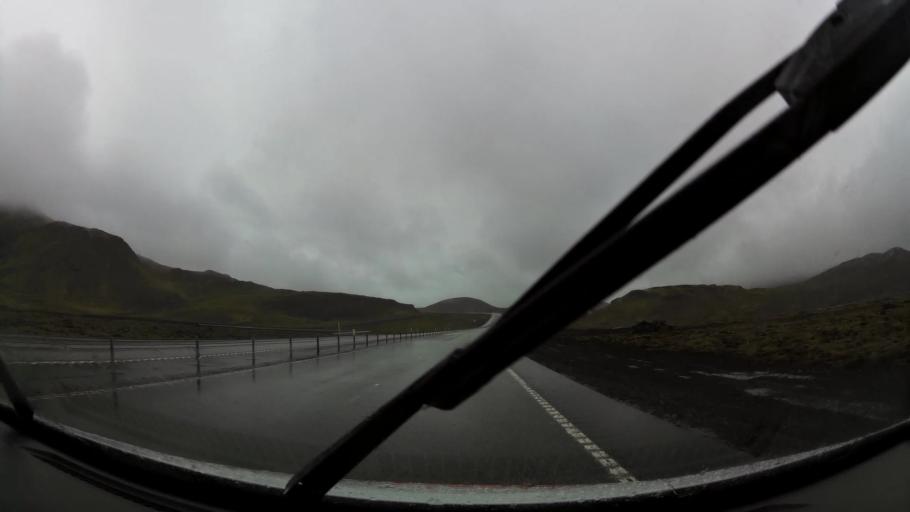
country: IS
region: South
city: THorlakshoefn
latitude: 64.0277
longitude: -21.4211
